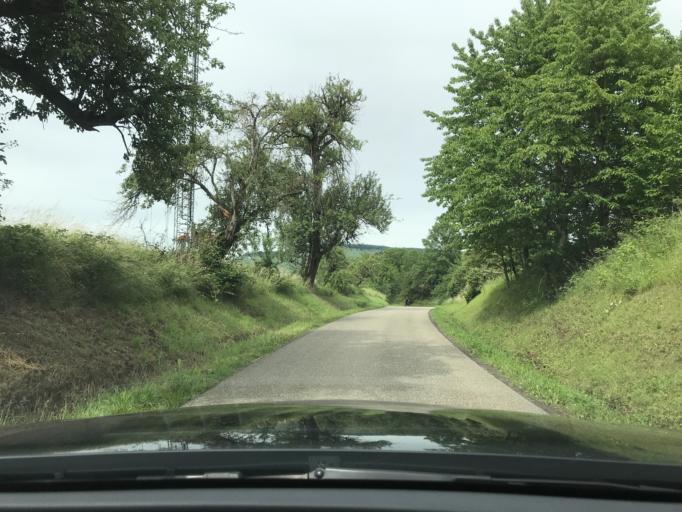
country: DE
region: Baden-Wuerttemberg
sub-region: Regierungsbezirk Stuttgart
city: Weinstadt-Endersbach
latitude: 48.8050
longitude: 9.3620
